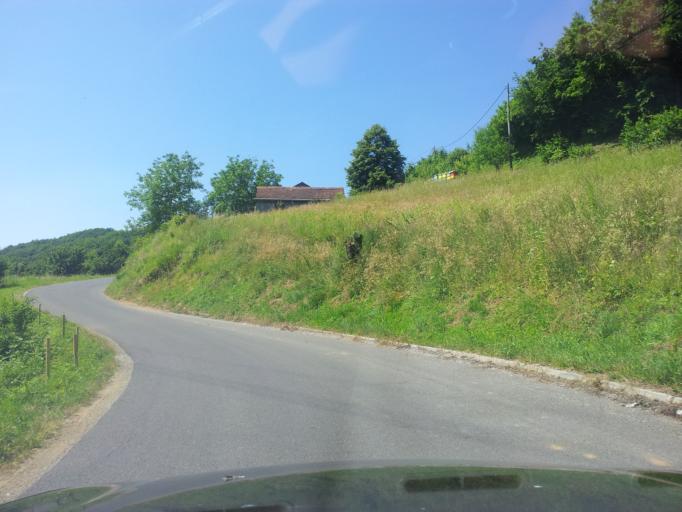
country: HR
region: Karlovacka
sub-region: Grad Karlovac
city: Karlovac
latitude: 45.4775
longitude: 15.4767
